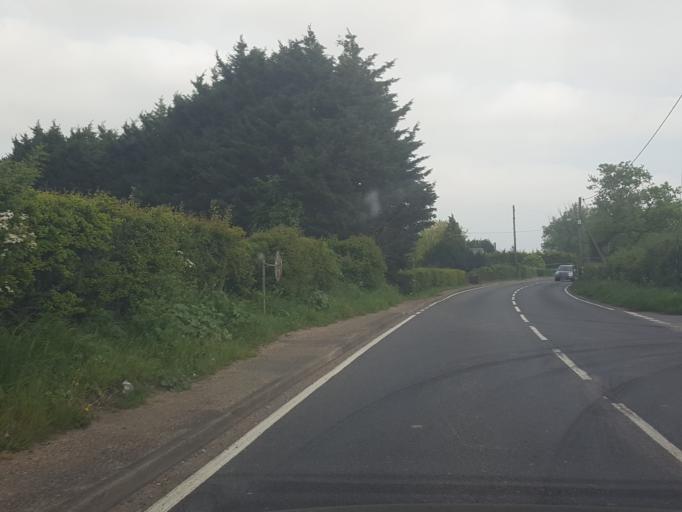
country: GB
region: England
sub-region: Essex
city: Little Clacton
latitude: 51.8543
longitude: 1.1793
